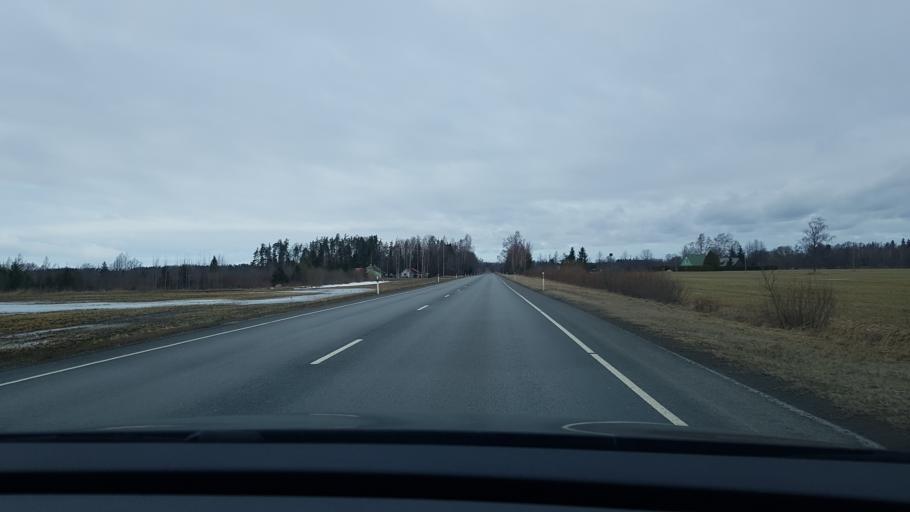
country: EE
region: Paernumaa
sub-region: Paikuse vald
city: Paikuse
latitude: 58.2251
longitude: 24.7036
